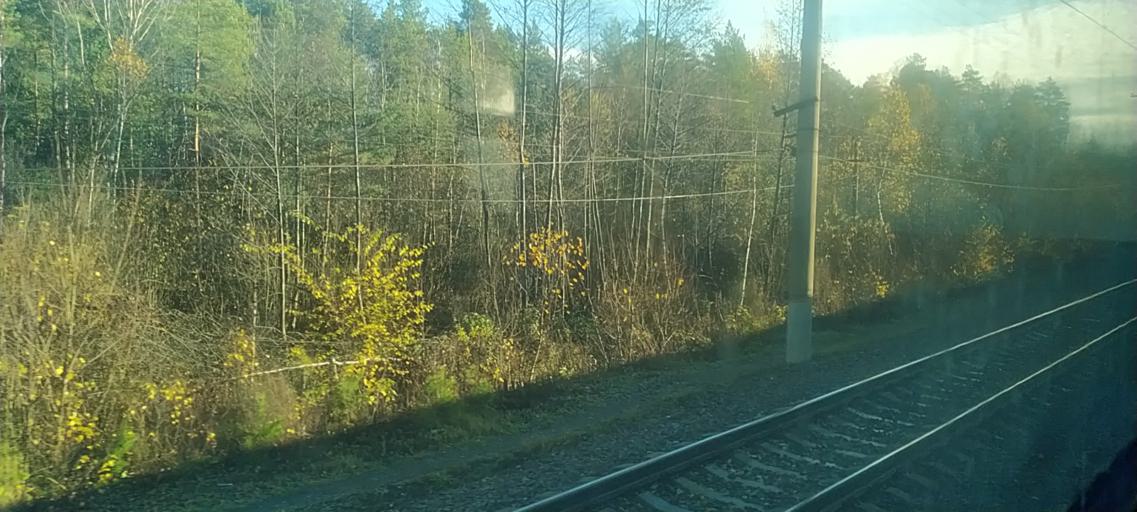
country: RU
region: Moskovskaya
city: Ramenskoye
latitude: 55.6386
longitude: 38.2604
